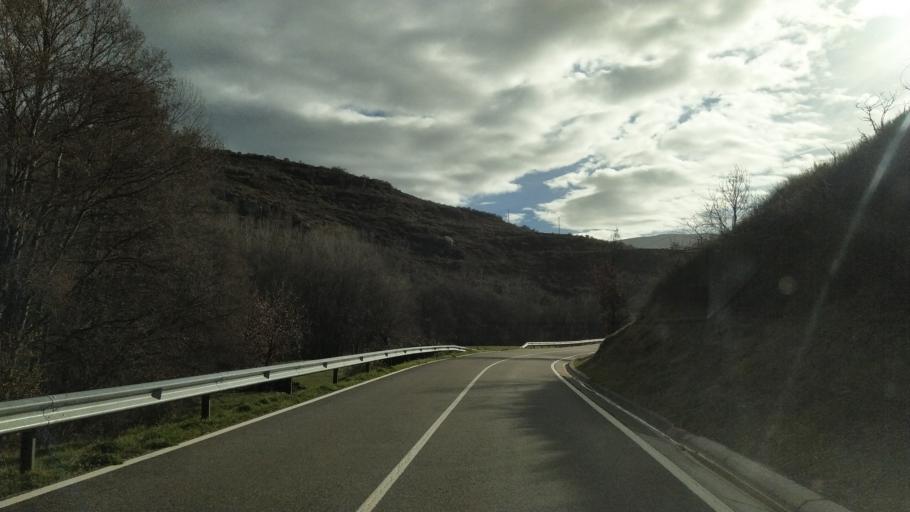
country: ES
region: Cantabria
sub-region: Provincia de Cantabria
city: San Martin de Elines
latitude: 42.8412
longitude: -3.9102
